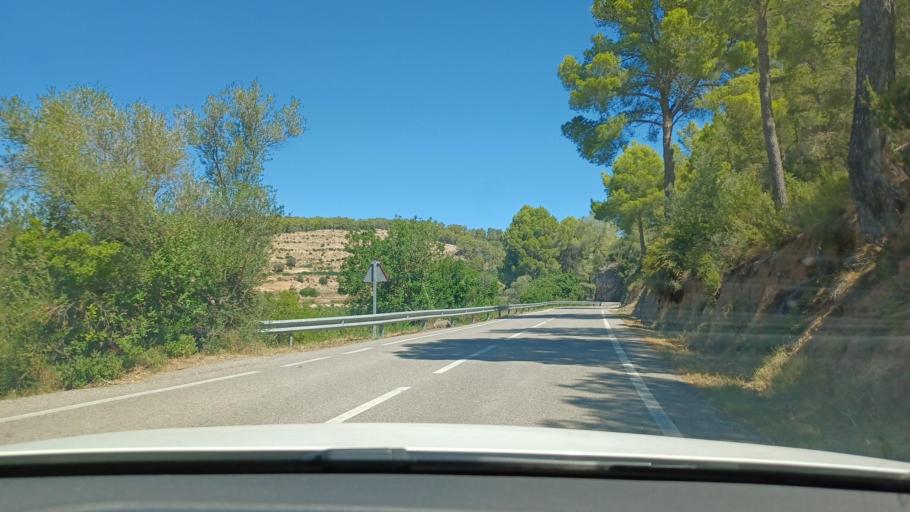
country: ES
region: Catalonia
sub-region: Provincia de Tarragona
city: Benifallet
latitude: 40.9546
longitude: 0.5037
